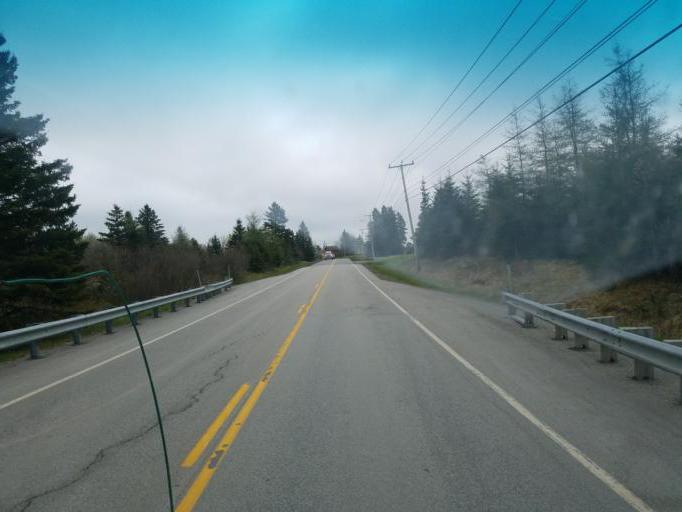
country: US
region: Maine
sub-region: Washington County
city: Eastport
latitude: 44.8208
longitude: -67.0523
